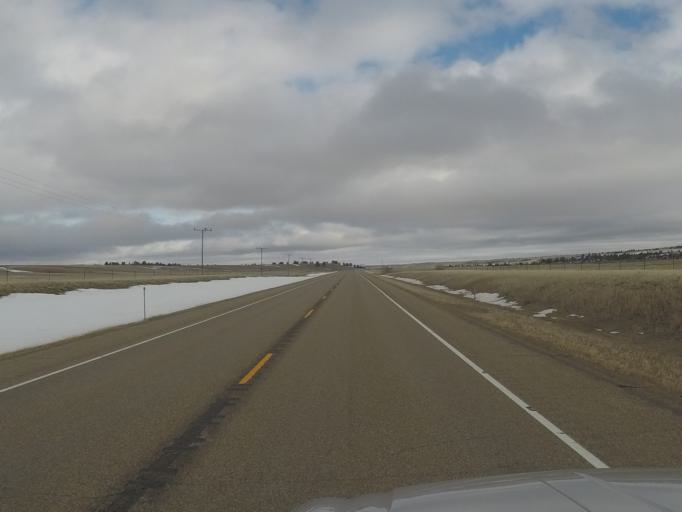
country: US
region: Montana
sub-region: Golden Valley County
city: Ryegate
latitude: 46.3249
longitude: -109.4549
